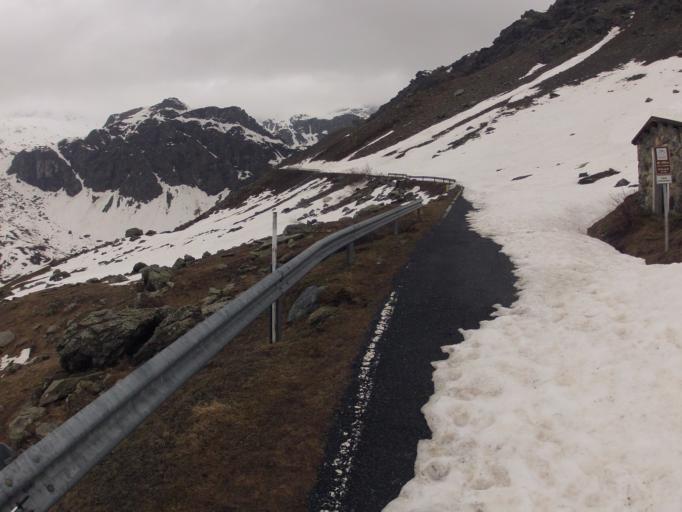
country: IT
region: Piedmont
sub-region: Provincia di Cuneo
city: Crissolo
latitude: 44.7038
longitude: 7.1086
